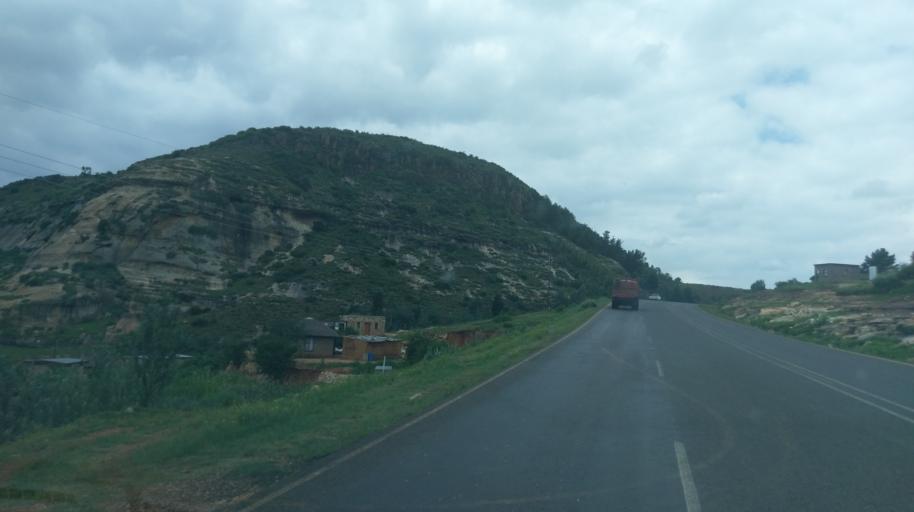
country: LS
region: Leribe
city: Leribe
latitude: -28.9899
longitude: 28.1872
